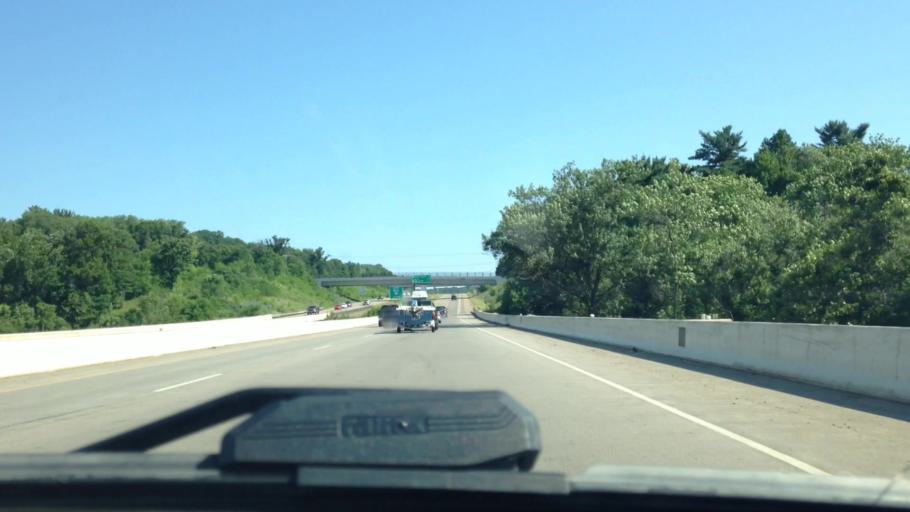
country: US
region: Wisconsin
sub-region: Eau Claire County
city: Altoona
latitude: 44.8230
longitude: -91.4539
